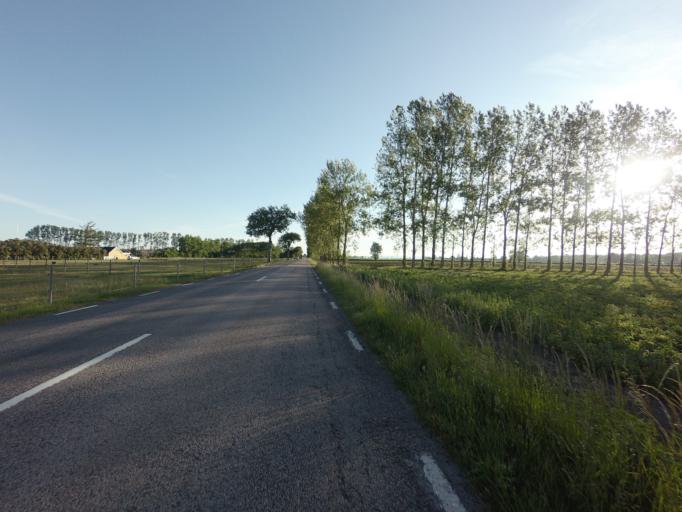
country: SE
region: Skane
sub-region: Hoganas Kommun
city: Hoganas
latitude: 56.2104
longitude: 12.6768
